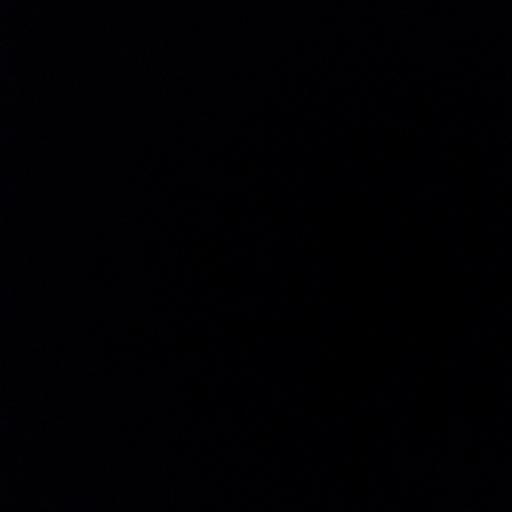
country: FI
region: Varsinais-Suomi
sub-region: Vakka-Suomi
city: Uusikaupunki
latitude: 60.7764
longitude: 21.3881
